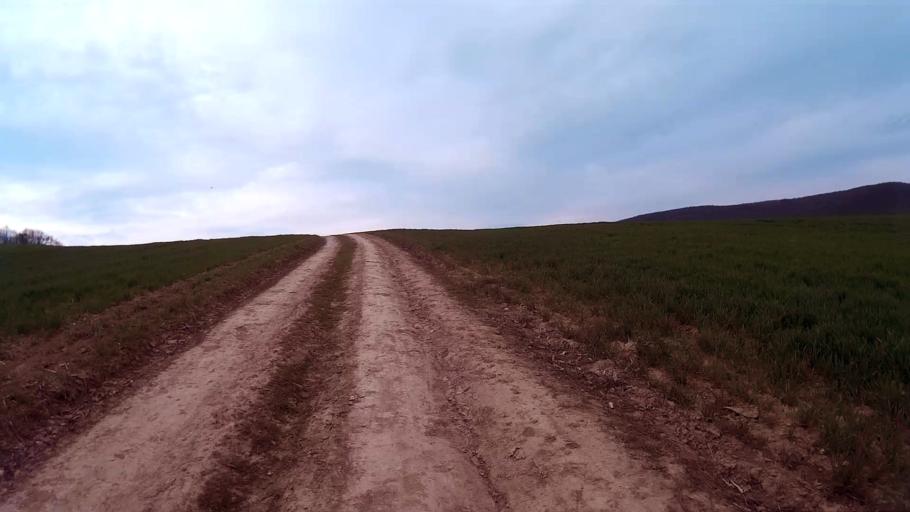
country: CZ
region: South Moravian
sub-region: Mesto Brno
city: Mokra Hora
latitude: 49.2434
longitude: 16.5451
